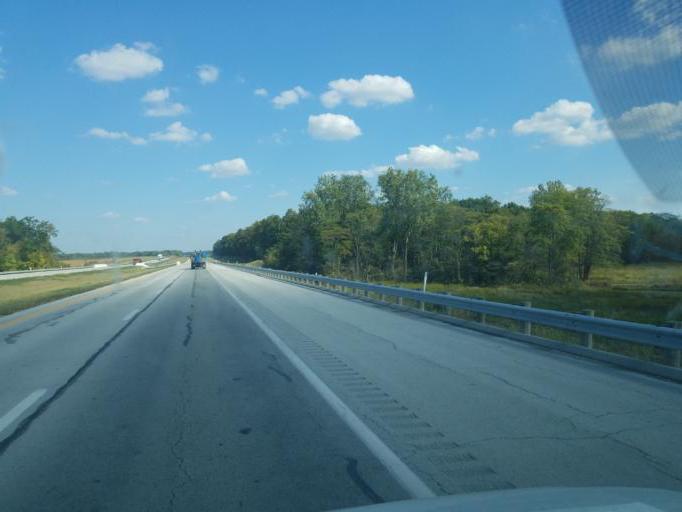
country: US
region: Ohio
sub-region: Wyandot County
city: Upper Sandusky
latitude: 40.8252
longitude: -83.3791
